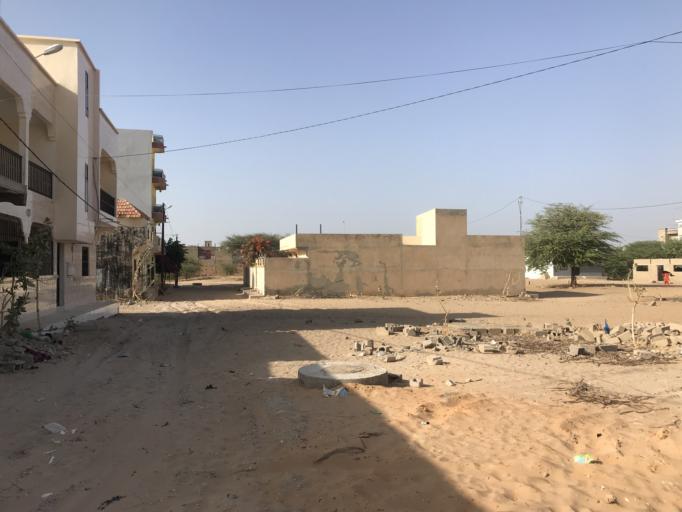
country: SN
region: Saint-Louis
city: Saint-Louis
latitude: 16.0365
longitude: -16.4426
